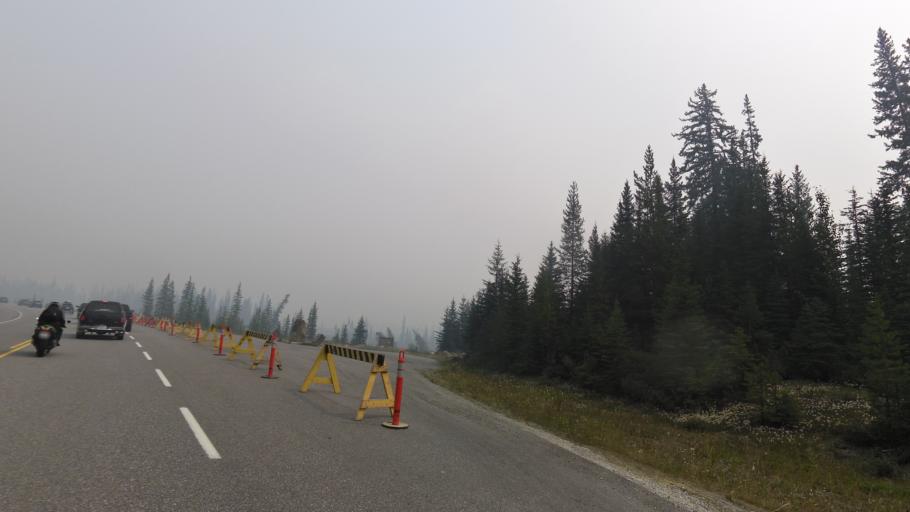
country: CA
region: Alberta
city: Banff
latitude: 50.9718
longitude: -115.9479
